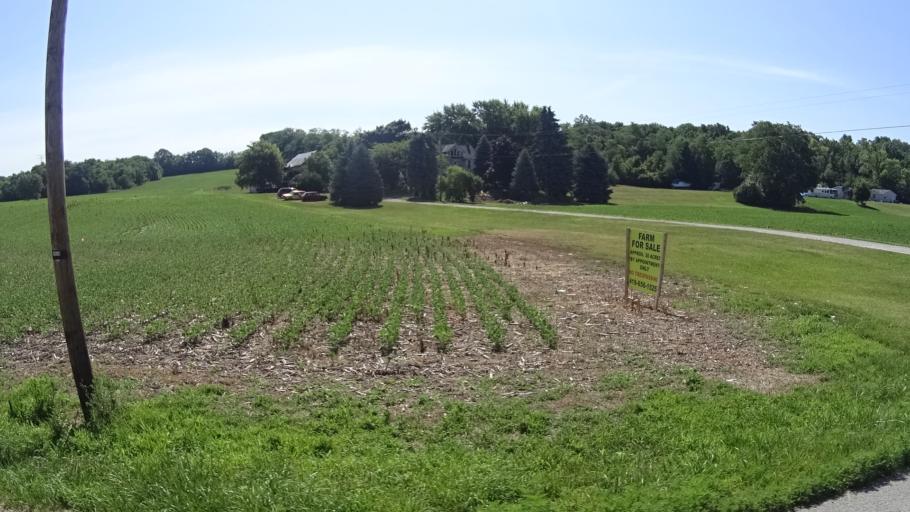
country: US
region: Ohio
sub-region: Huron County
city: Bellevue
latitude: 41.3842
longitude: -82.8366
